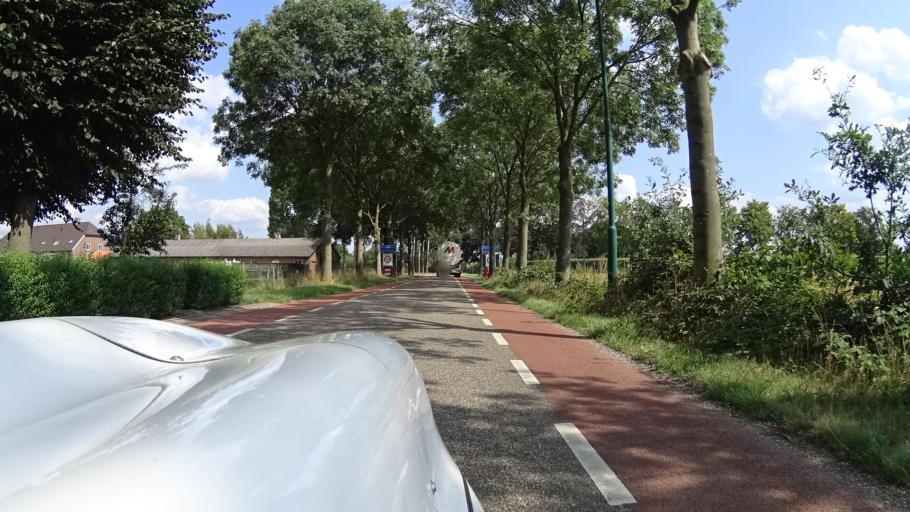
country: NL
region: North Brabant
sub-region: Gemeente Veghel
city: Veghel
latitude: 51.6511
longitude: 5.5445
